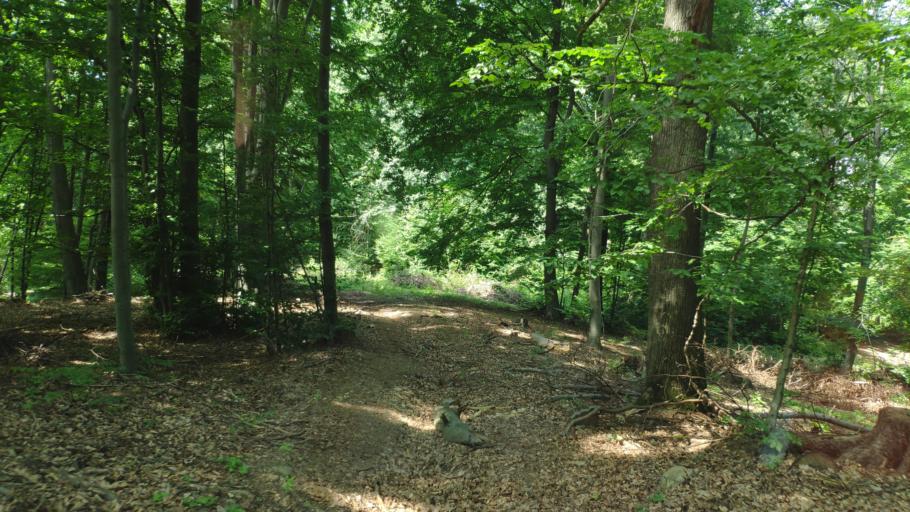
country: SK
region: Kosicky
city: Dobsina
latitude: 48.7077
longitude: 20.3812
